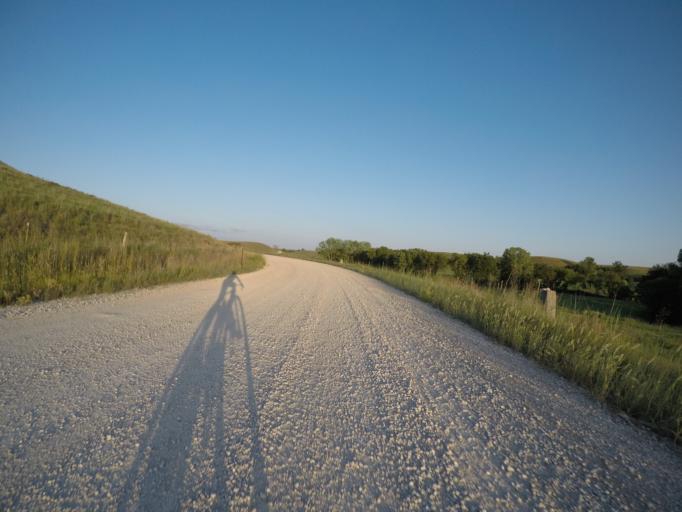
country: US
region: Kansas
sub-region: Riley County
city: Ogden
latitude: 39.0122
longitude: -96.6541
